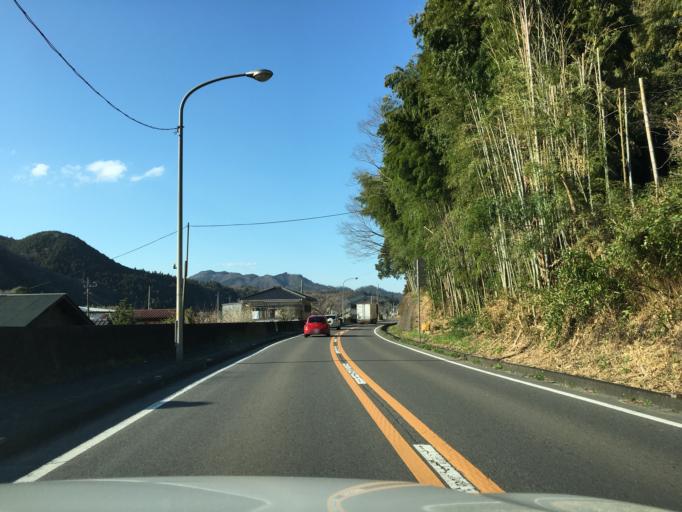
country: JP
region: Ibaraki
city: Daigo
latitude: 36.6999
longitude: 140.3839
